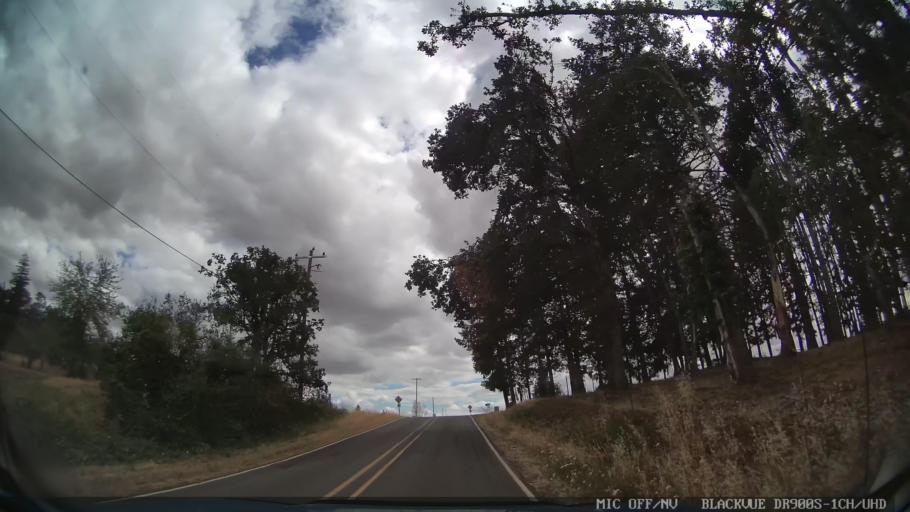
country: US
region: Oregon
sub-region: Marion County
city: Sublimity
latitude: 44.8433
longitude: -122.7741
